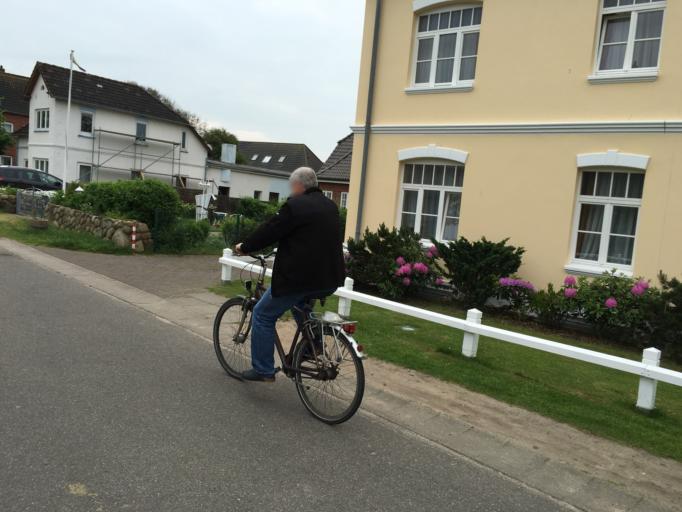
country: DE
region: Schleswig-Holstein
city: Norddorf
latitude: 54.6794
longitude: 8.3341
